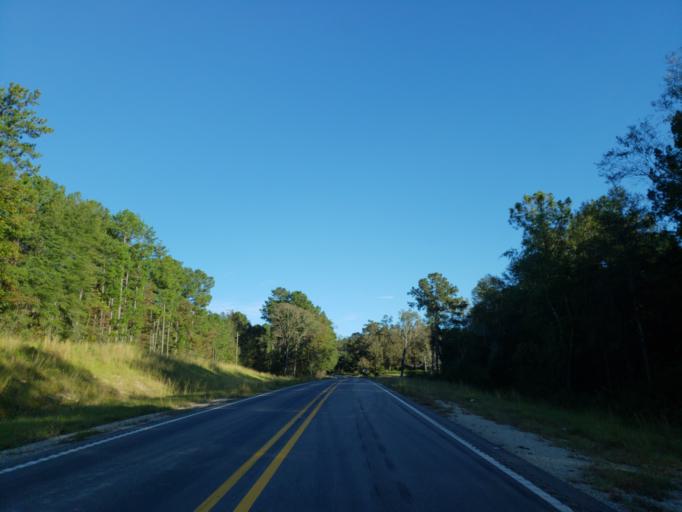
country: US
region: Mississippi
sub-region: Perry County
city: Richton
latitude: 31.3630
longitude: -88.8045
